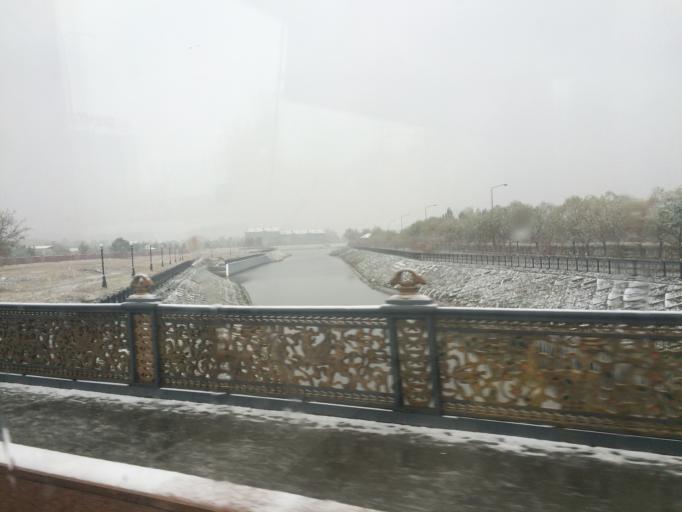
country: KZ
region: Astana Qalasy
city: Astana
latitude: 51.1505
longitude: 71.4445
